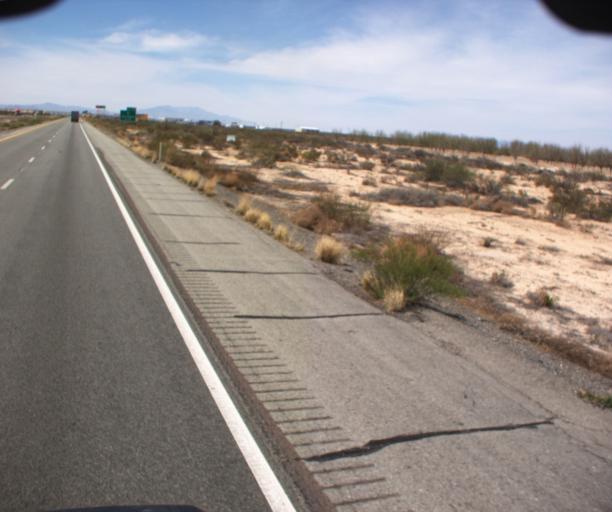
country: US
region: New Mexico
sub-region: Hidalgo County
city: Lordsburg
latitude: 32.2664
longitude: -109.2374
